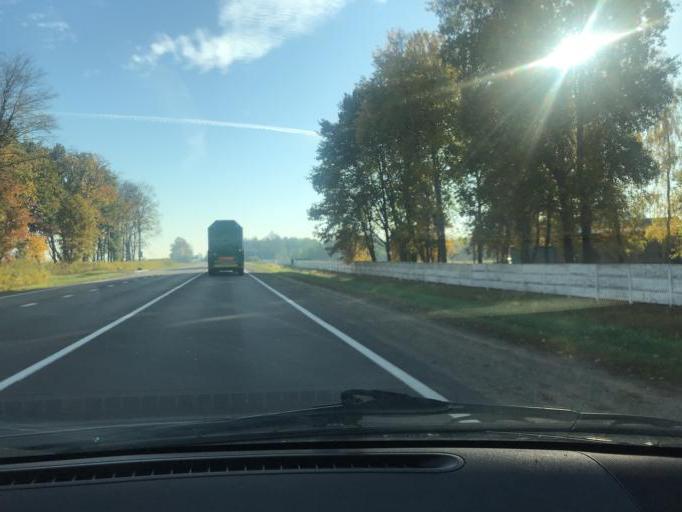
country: BY
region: Brest
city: Ivanava
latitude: 52.1499
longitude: 25.3911
